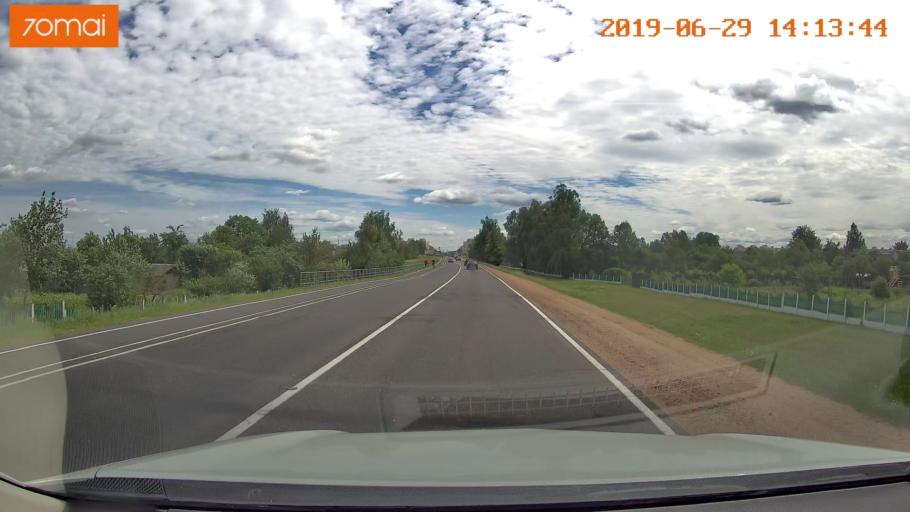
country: BY
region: Minsk
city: Salihorsk
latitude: 52.8008
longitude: 27.5121
